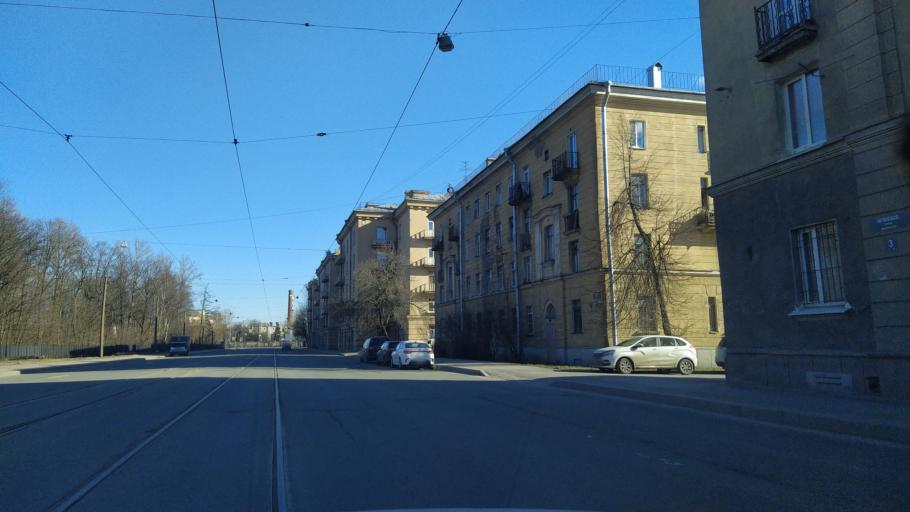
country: RU
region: St.-Petersburg
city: Centralniy
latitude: 59.9013
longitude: 30.3663
